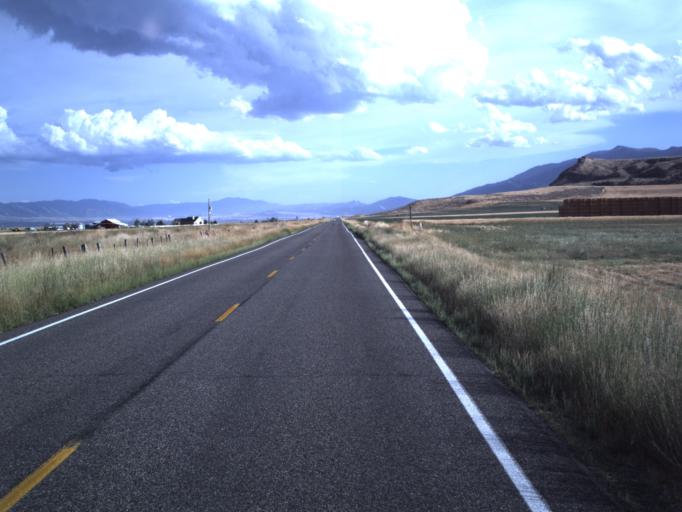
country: US
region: Utah
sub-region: Cache County
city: Benson
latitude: 41.8226
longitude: -111.9990
